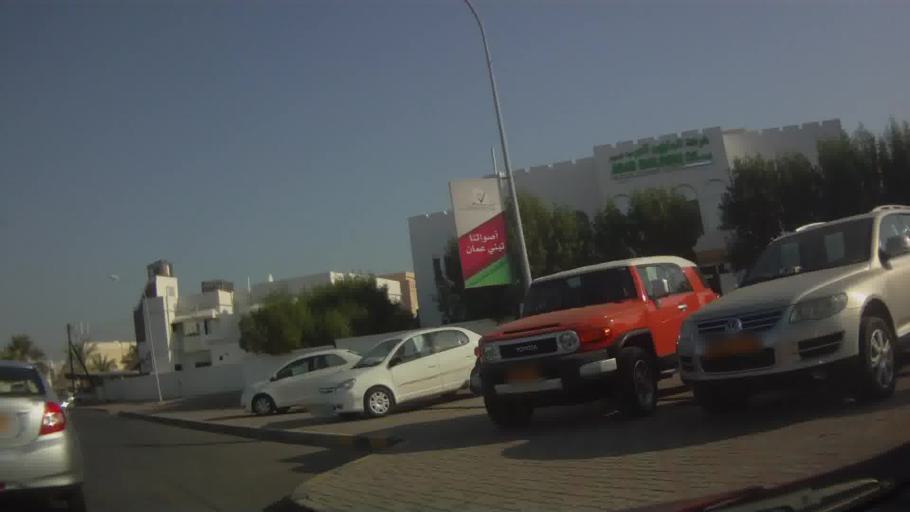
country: OM
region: Muhafazat Masqat
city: Bawshar
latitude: 23.5908
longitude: 58.4180
